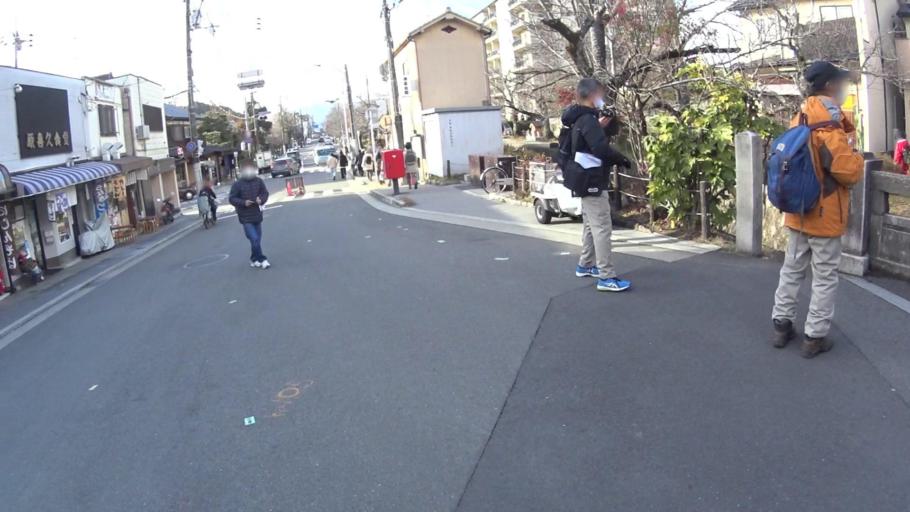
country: JP
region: Kyoto
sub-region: Kyoto-shi
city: Kamigyo-ku
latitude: 35.0241
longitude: 135.8025
